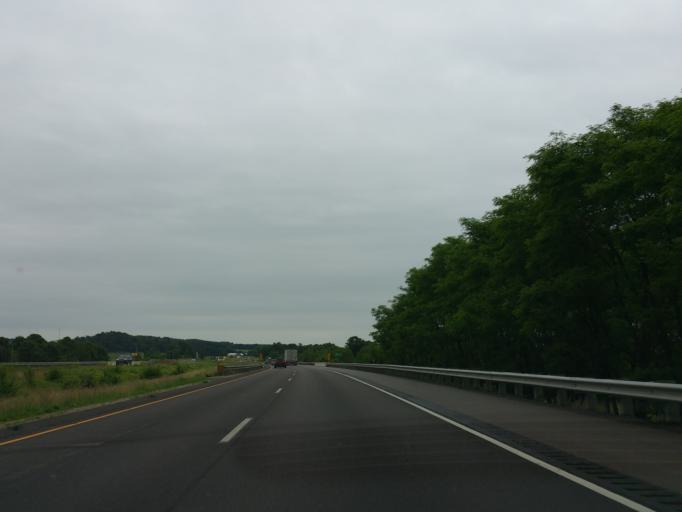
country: US
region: Wisconsin
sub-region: Eau Claire County
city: Fall Creek
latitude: 44.7308
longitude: -91.3659
